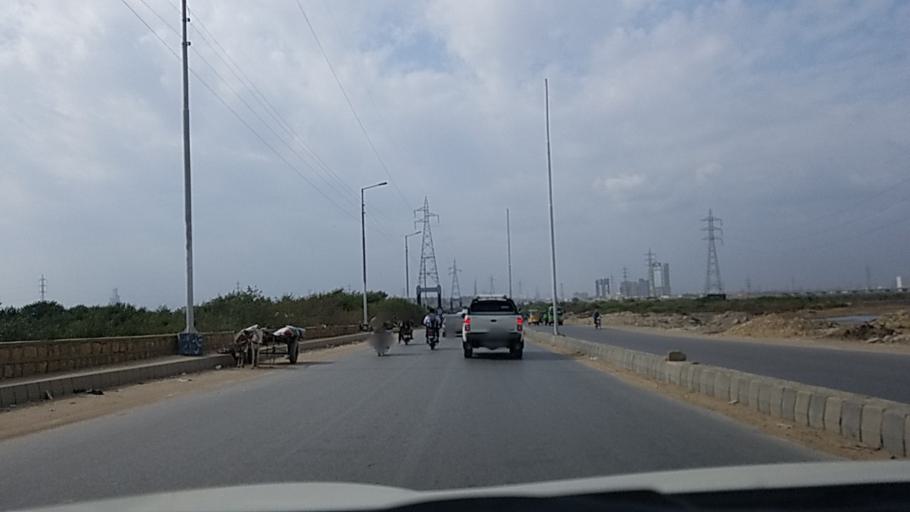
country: PK
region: Sindh
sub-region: Karachi District
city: Karachi
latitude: 24.8215
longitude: 67.0993
